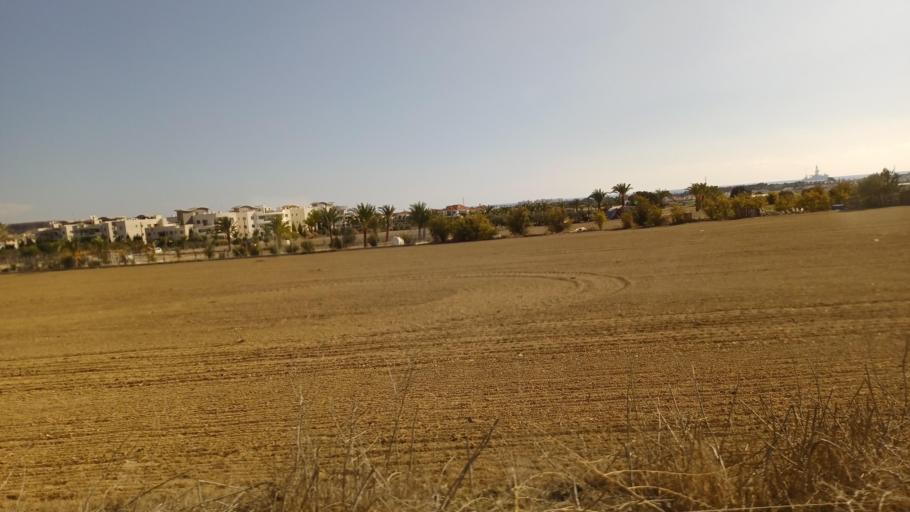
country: CY
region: Larnaka
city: Voroklini
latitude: 34.9963
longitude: 33.6710
